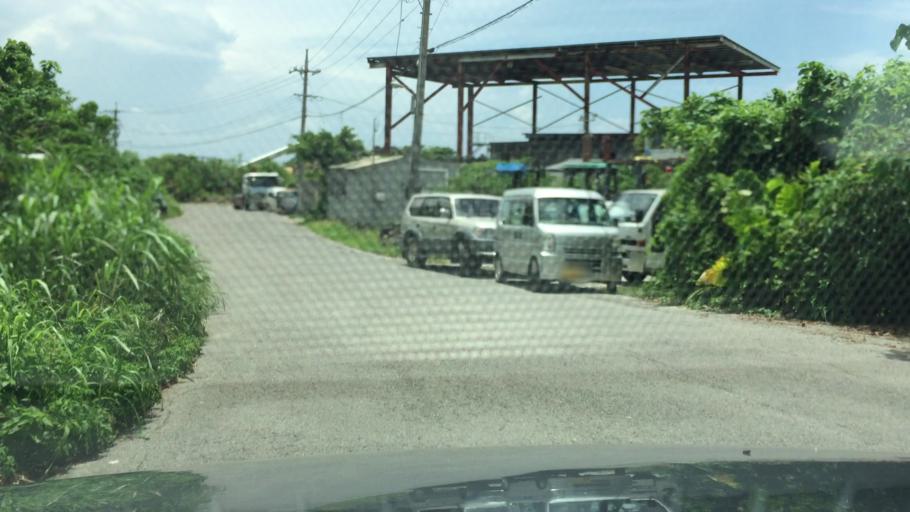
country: JP
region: Okinawa
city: Ishigaki
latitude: 24.3599
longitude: 124.1545
